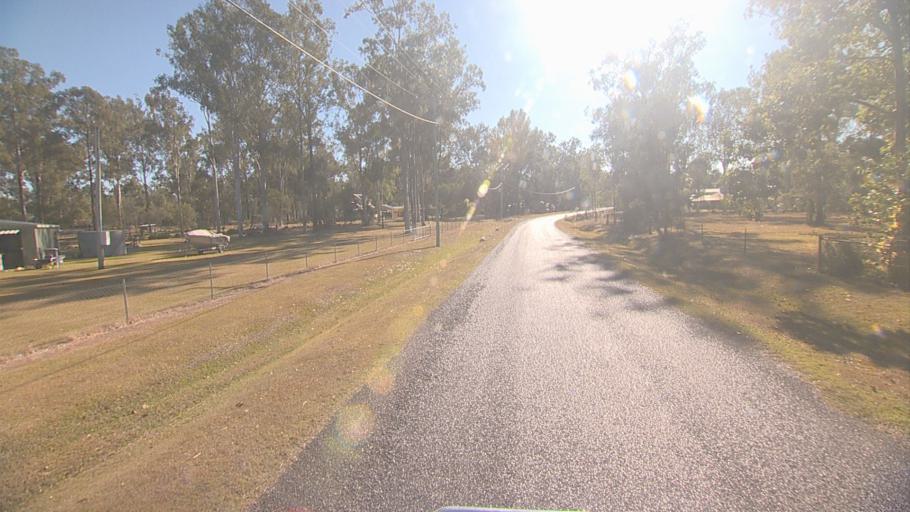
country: AU
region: Queensland
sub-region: Logan
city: North Maclean
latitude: -27.8066
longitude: 152.9884
